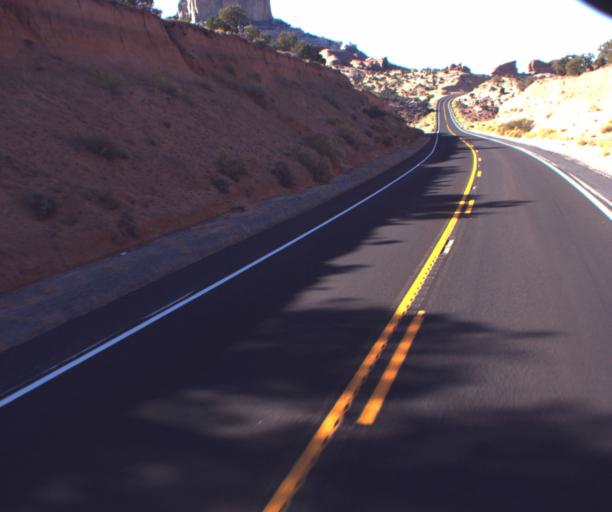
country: US
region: Arizona
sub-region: Coconino County
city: Kaibito
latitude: 36.6006
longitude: -110.9144
